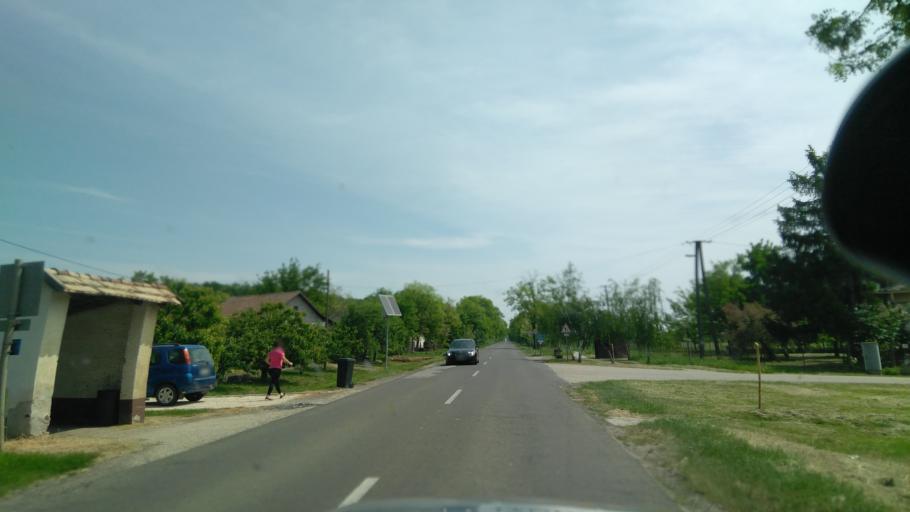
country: HU
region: Csongrad
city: Fabiansebestyen
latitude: 46.5756
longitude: 20.4423
